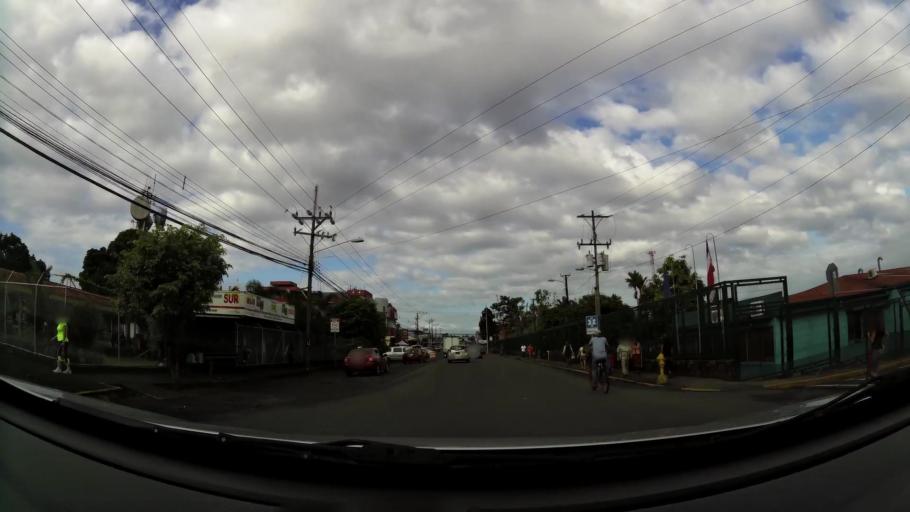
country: CR
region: Limon
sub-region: Canton de Pococi
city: Guapiles
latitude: 10.2161
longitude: -83.7887
